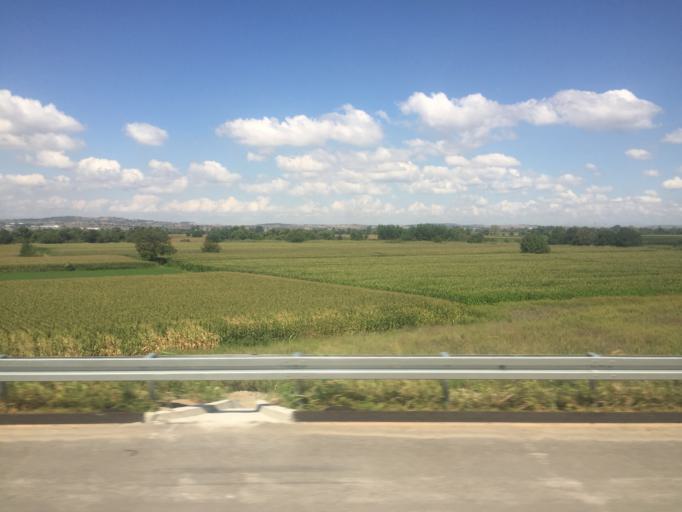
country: TR
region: Balikesir
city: Gobel
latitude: 40.0231
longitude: 28.2069
